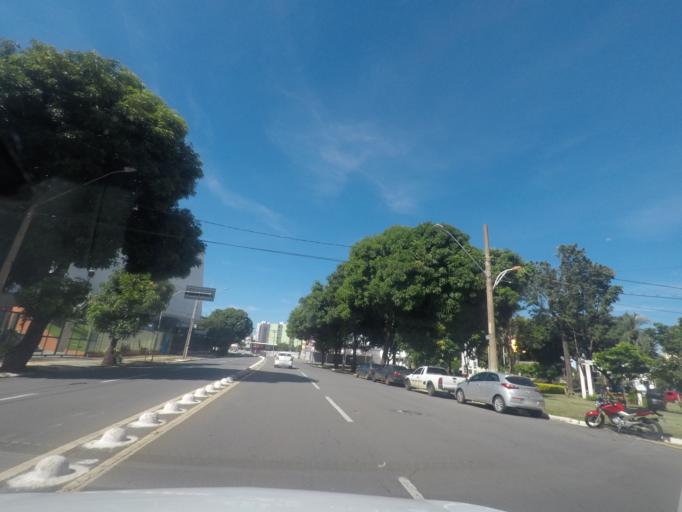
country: BR
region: Goias
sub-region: Goiania
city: Goiania
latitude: -16.6743
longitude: -49.2648
